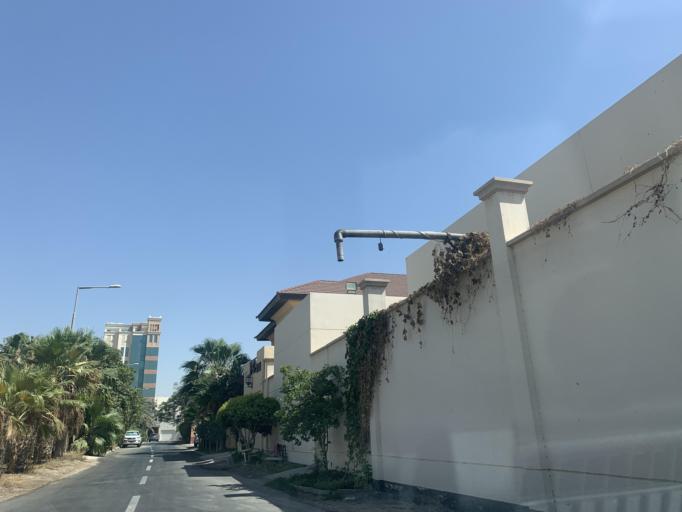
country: BH
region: Manama
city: Jidd Hafs
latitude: 26.2235
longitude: 50.5014
